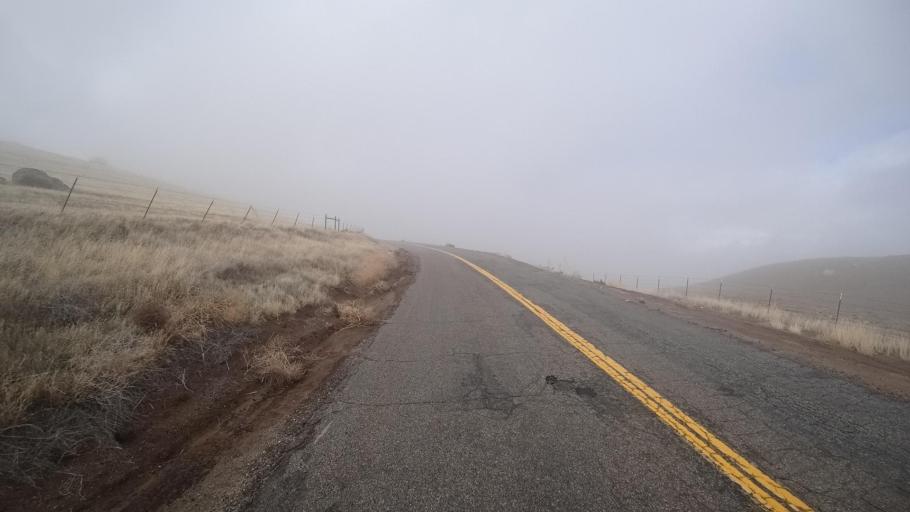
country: US
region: California
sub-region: Kern County
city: Maricopa
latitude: 34.9284
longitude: -119.4106
